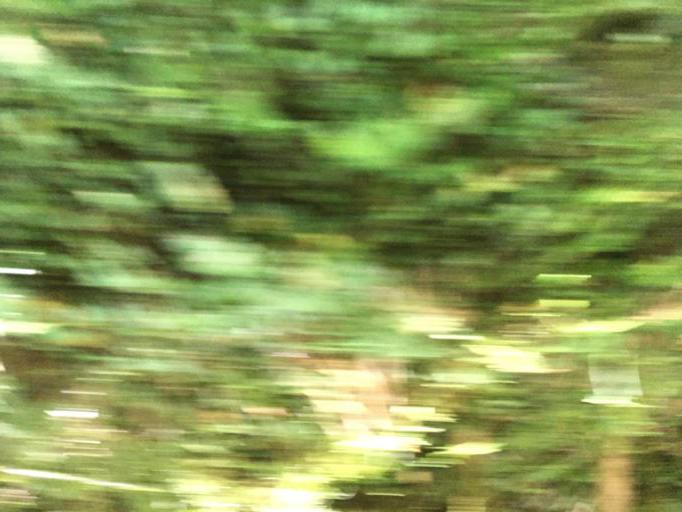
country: TW
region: Taiwan
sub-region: Yilan
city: Yilan
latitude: 24.6215
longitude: 121.4795
